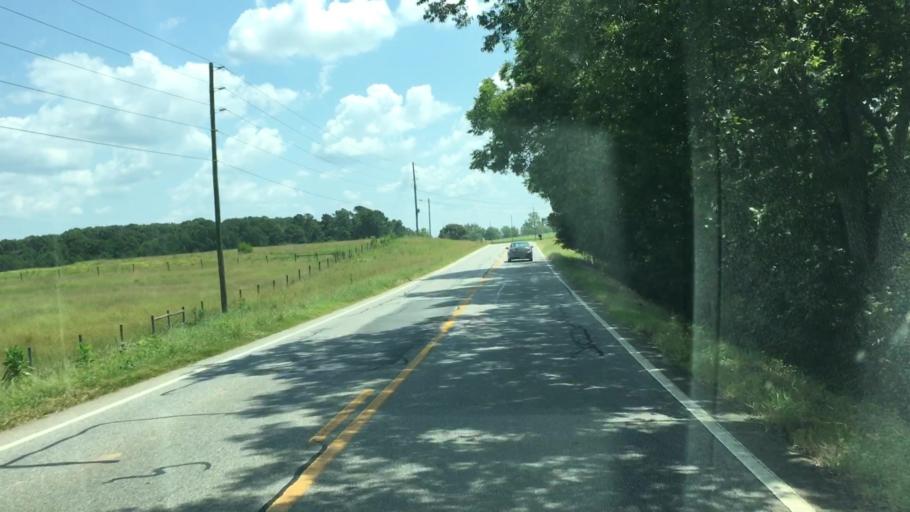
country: US
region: Georgia
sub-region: Barrow County
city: Statham
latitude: 33.9495
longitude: -83.6503
